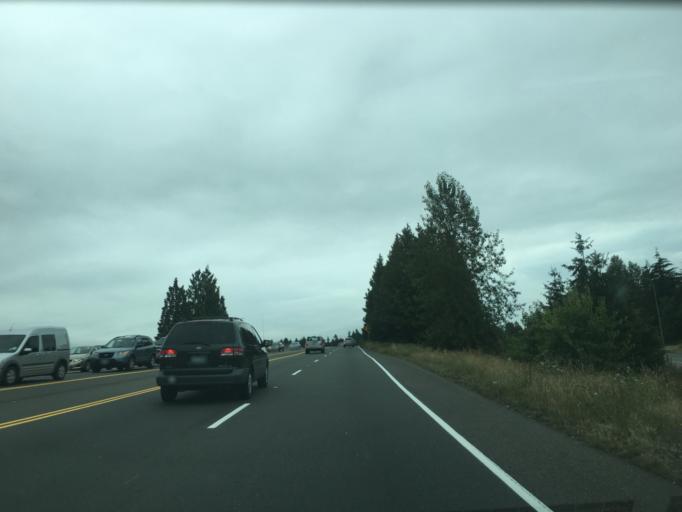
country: US
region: Washington
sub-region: King County
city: Kingsgate
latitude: 47.7109
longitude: -122.1851
